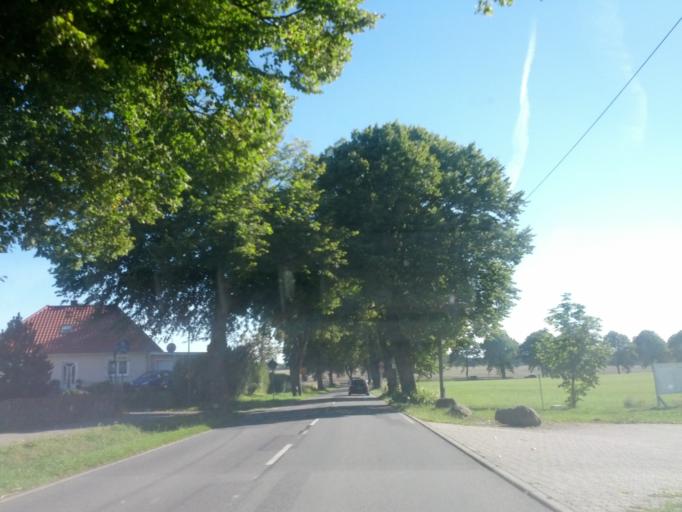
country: DE
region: Mecklenburg-Vorpommern
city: Bastorf
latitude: 54.1249
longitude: 11.6931
